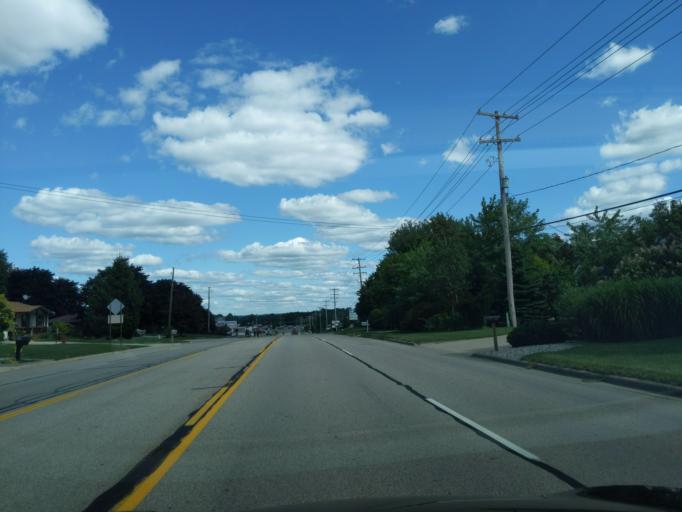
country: US
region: Michigan
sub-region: Kent County
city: Comstock Park
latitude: 43.0291
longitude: -85.6980
